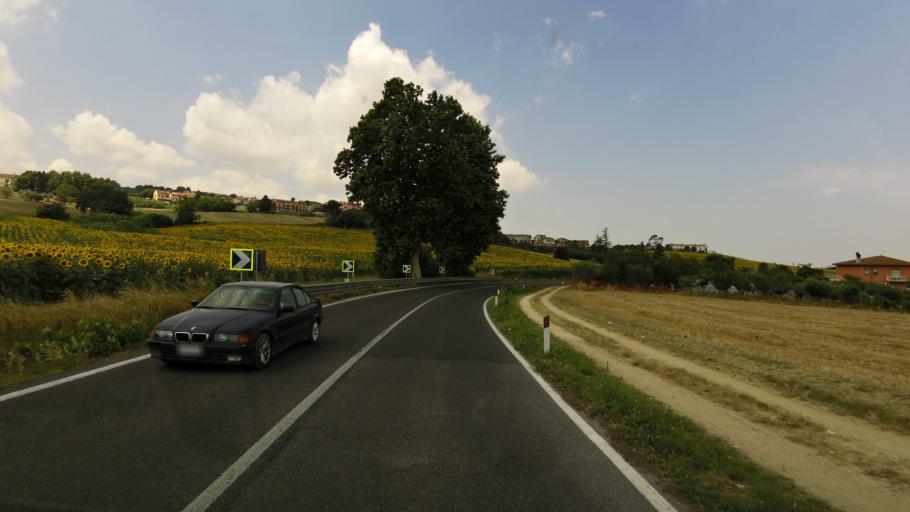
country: IT
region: The Marches
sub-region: Provincia di Ancona
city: Castelfidardo
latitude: 43.4846
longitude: 13.5758
